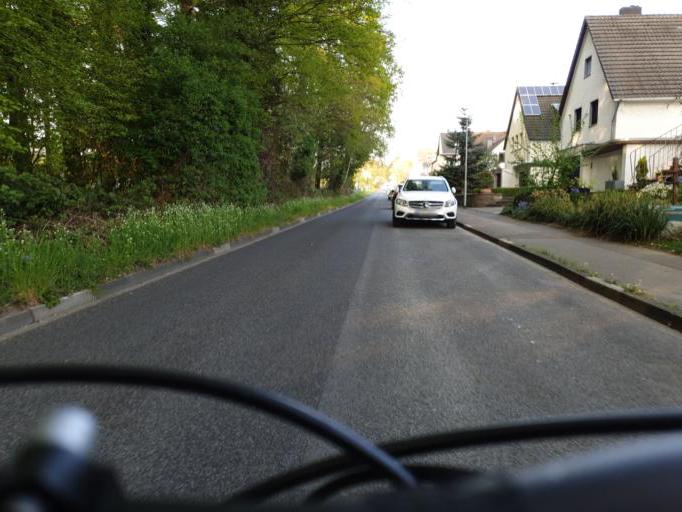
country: DE
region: North Rhine-Westphalia
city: Opladen
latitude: 51.0477
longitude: 7.0501
